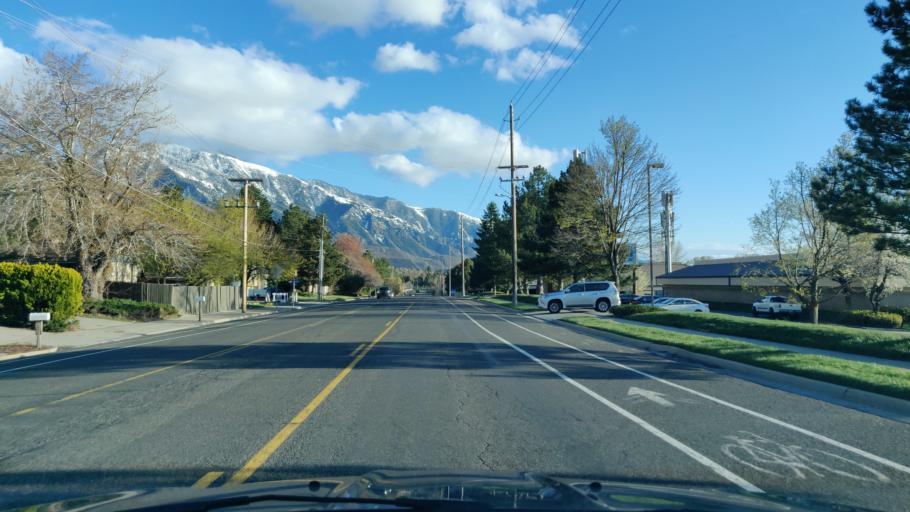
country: US
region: Utah
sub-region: Salt Lake County
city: Cottonwood Heights
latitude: 40.6088
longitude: -111.7960
